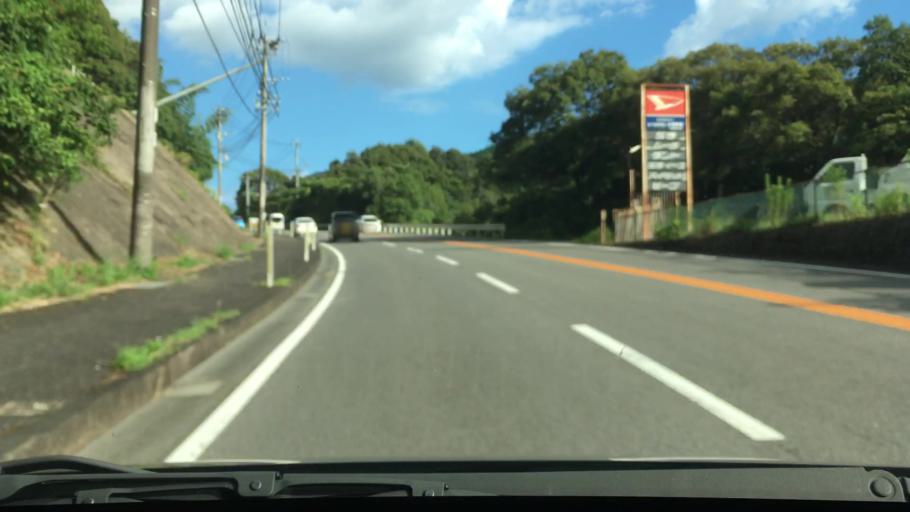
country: JP
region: Nagasaki
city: Togitsu
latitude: 32.8202
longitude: 129.8005
